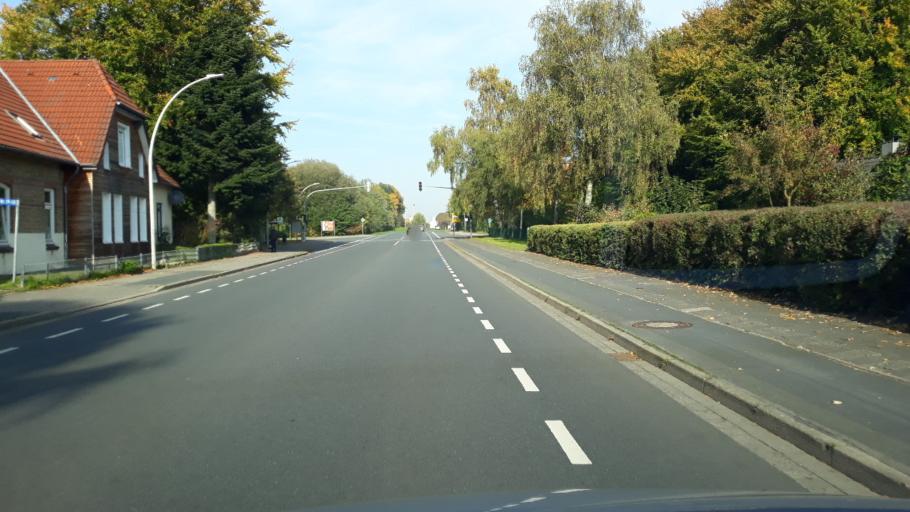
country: DE
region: Schleswig-Holstein
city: Schleswig
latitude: 54.5277
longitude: 9.5713
